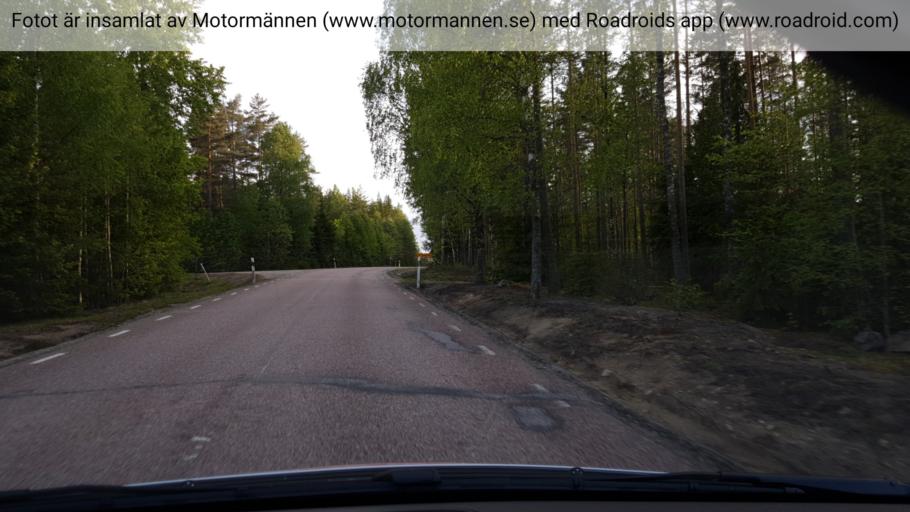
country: SE
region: Vaestmanland
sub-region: Skinnskattebergs Kommun
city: Skinnskatteberg
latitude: 59.8344
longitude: 15.8376
